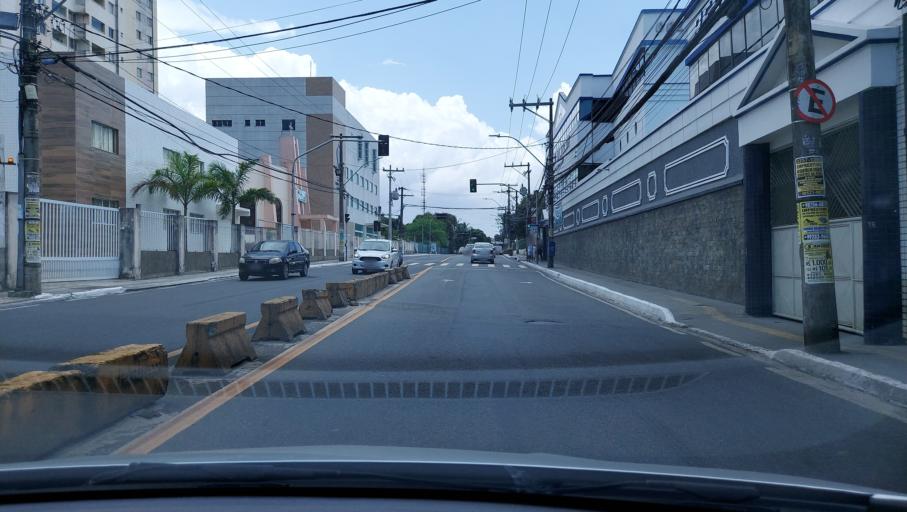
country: BR
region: Bahia
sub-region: Salvador
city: Salvador
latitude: -12.9649
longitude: -38.4725
